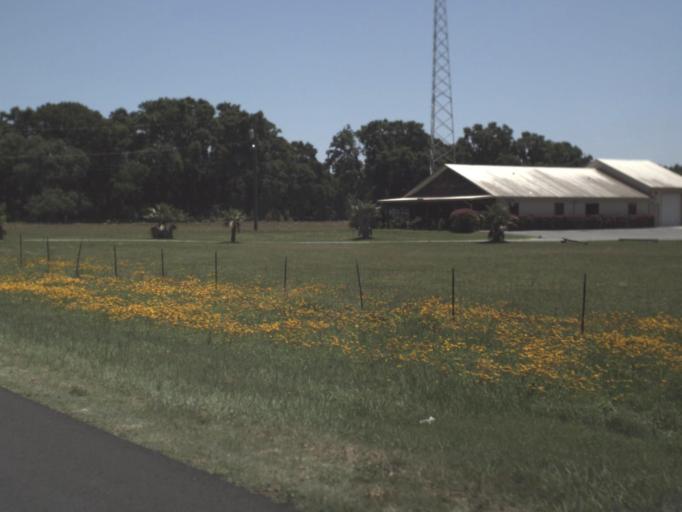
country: US
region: Florida
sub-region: Suwannee County
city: Wellborn
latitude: 30.2017
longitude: -82.7799
